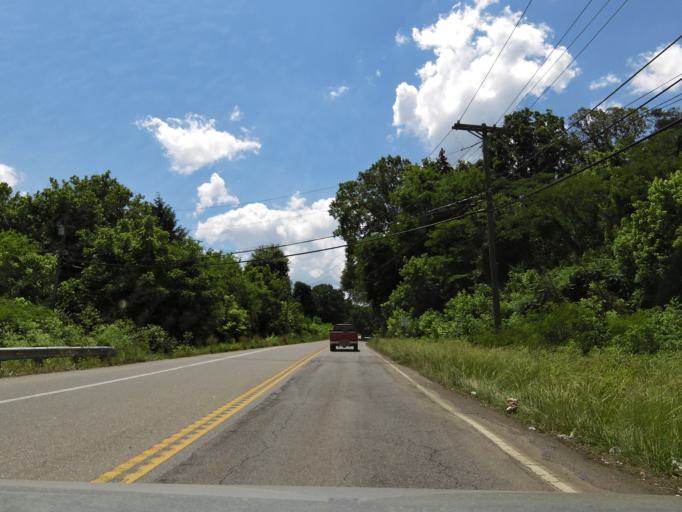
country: US
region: Tennessee
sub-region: Blount County
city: Maryville
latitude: 35.6965
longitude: -84.0441
